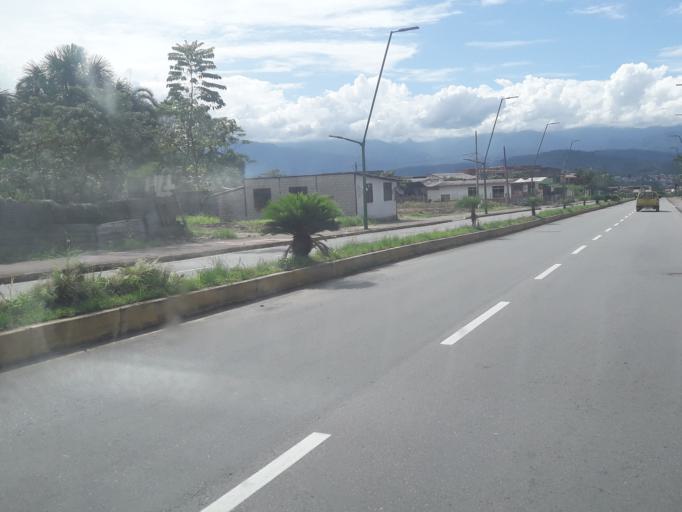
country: EC
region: Napo
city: Tena
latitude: -1.0137
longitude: -77.8084
